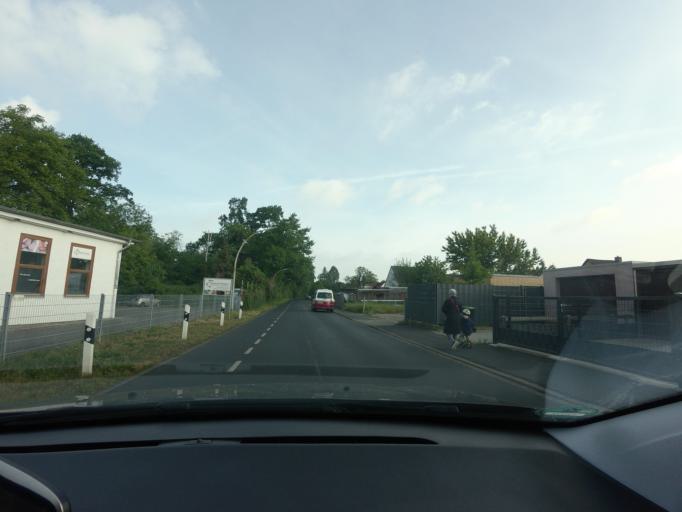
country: DE
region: Lower Saxony
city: Braunschweig
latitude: 52.3045
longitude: 10.5386
